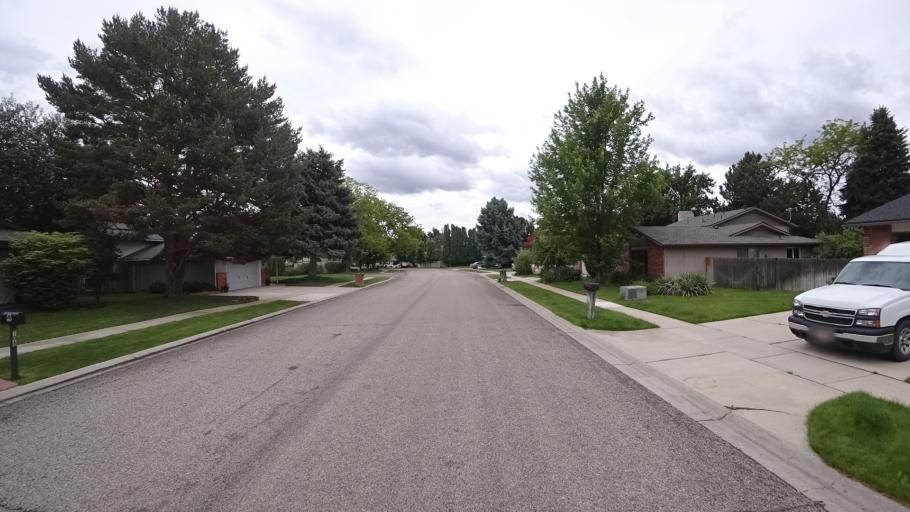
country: US
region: Idaho
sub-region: Ada County
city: Eagle
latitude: 43.7005
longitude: -116.3387
